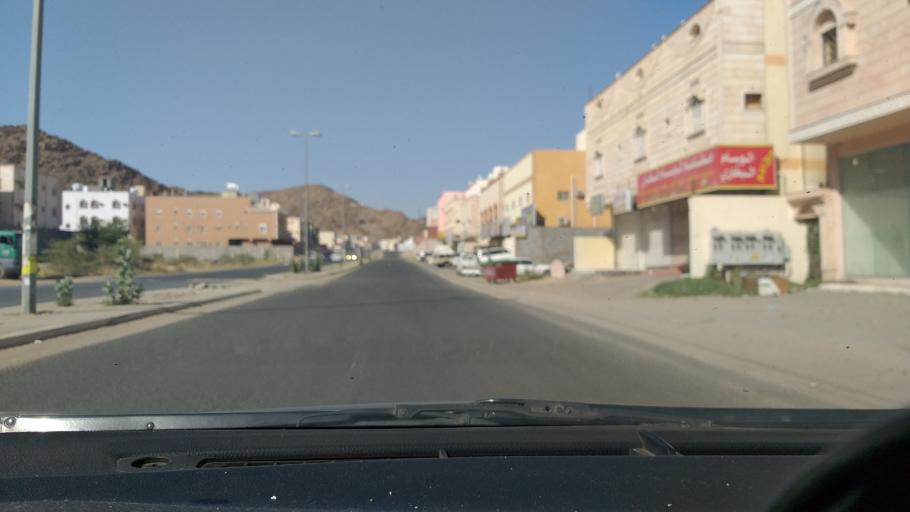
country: SA
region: Makkah
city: Ta'if
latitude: 21.2252
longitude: 40.3757
